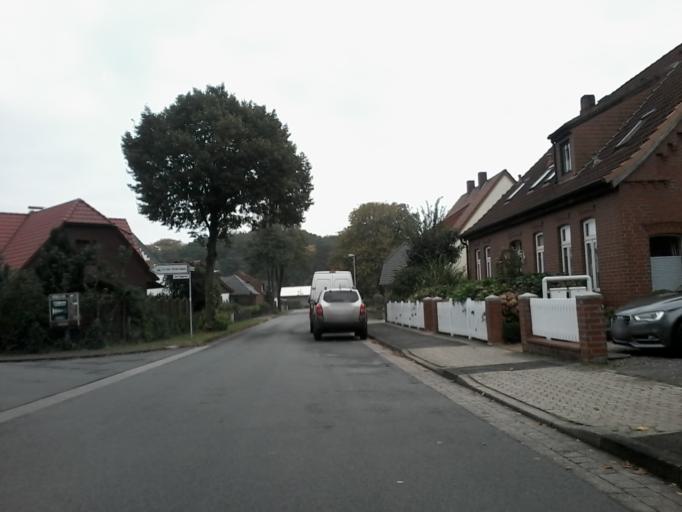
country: DE
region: Lower Saxony
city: Ahsen-Oetzen
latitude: 53.0032
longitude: 9.0843
